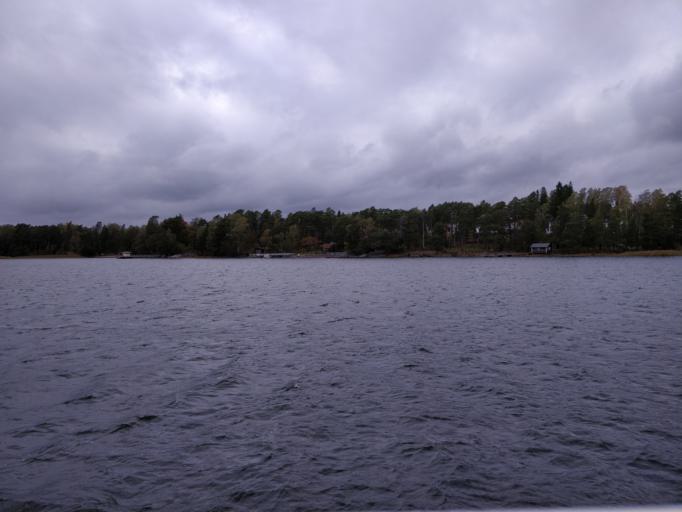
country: FI
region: Uusimaa
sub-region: Helsinki
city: Vantaa
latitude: 60.1579
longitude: 25.0942
